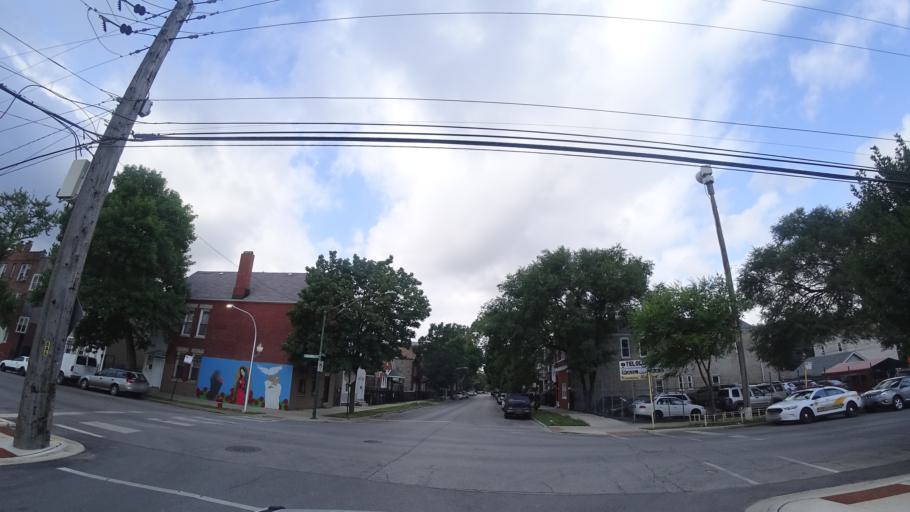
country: US
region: Illinois
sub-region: Cook County
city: Chicago
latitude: 41.8484
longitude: -87.6902
